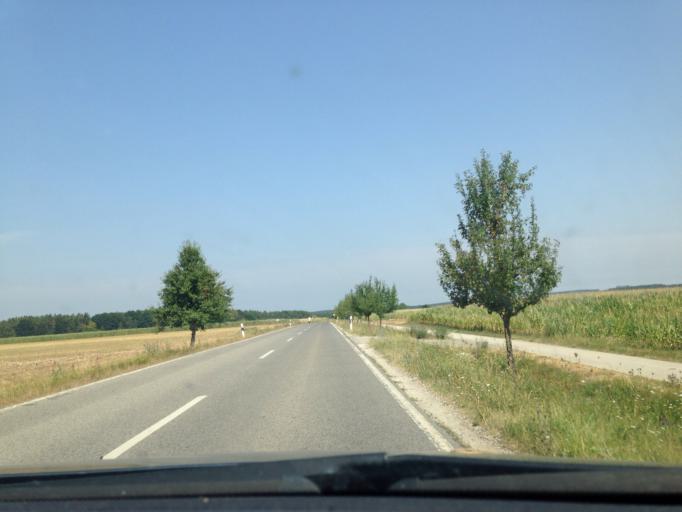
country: DE
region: Bavaria
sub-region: Regierungsbezirk Mittelfranken
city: Thalmassing
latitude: 49.1394
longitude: 11.2135
